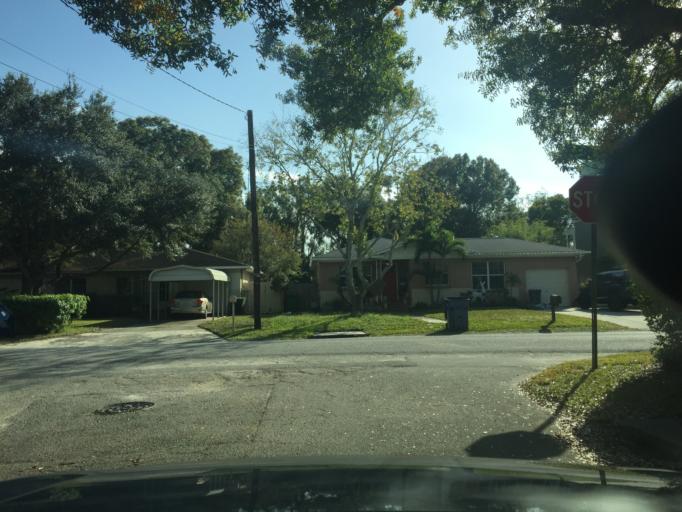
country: US
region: Florida
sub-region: Hillsborough County
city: Tampa
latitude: 27.9486
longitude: -82.4944
